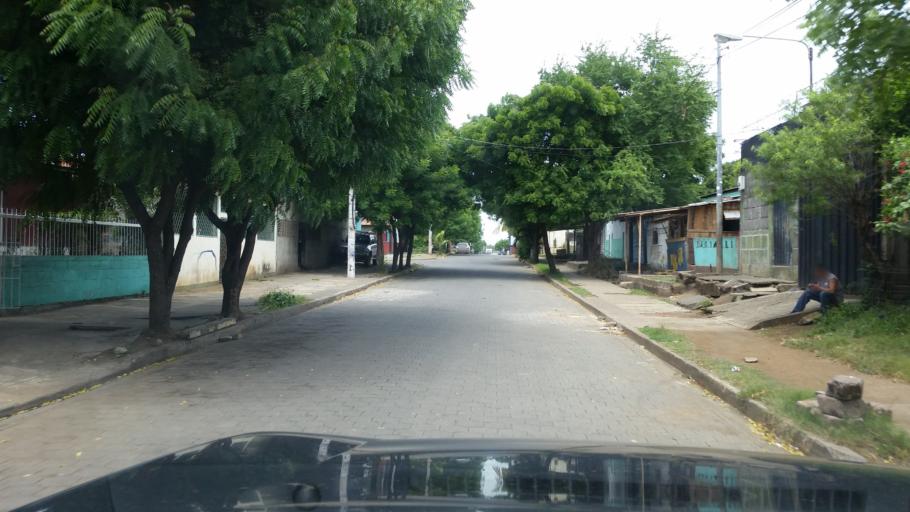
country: NI
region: Managua
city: Managua
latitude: 12.1472
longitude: -86.2156
